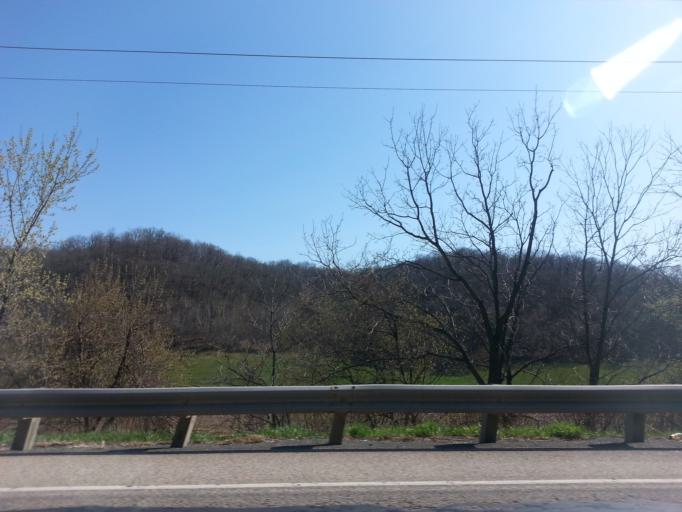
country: US
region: Wisconsin
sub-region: Pepin County
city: Durand
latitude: 44.6406
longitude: -92.0987
